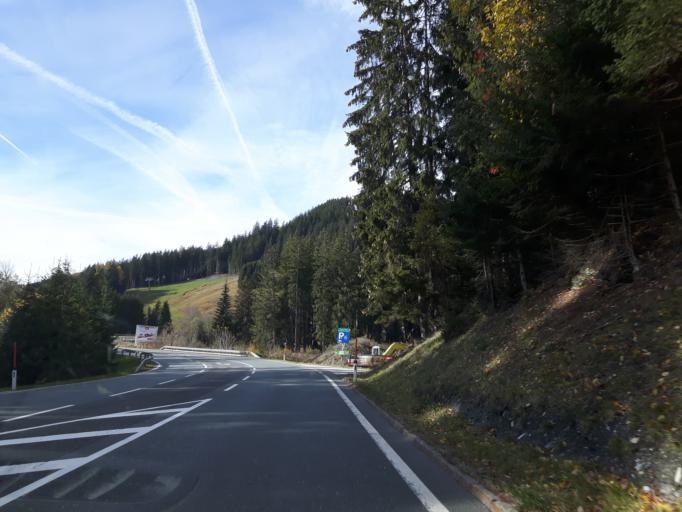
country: AT
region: Salzburg
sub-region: Politischer Bezirk Zell am See
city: Hollersbach im Pinzgau
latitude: 47.3004
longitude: 12.4133
